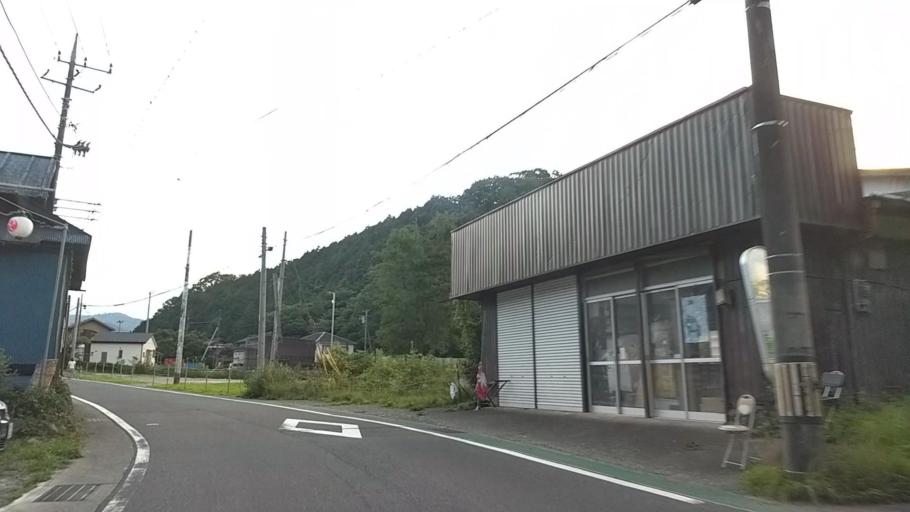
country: JP
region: Yamanashi
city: Uenohara
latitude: 35.5500
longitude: 139.2236
